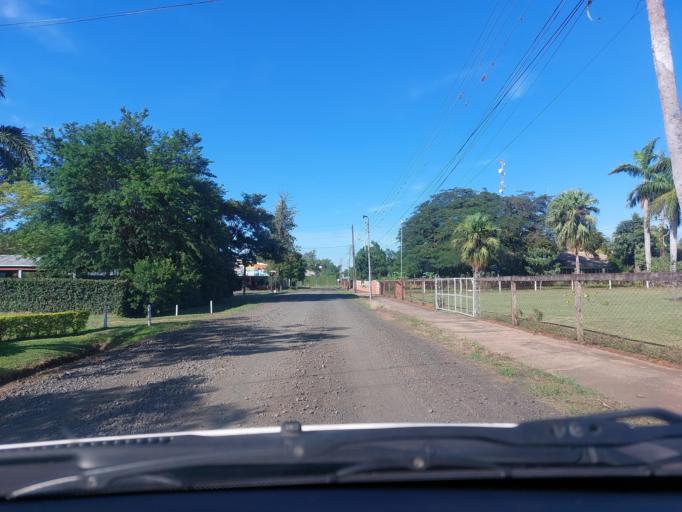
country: PY
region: San Pedro
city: Itacurubi del Rosario
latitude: -24.6113
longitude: -56.7951
